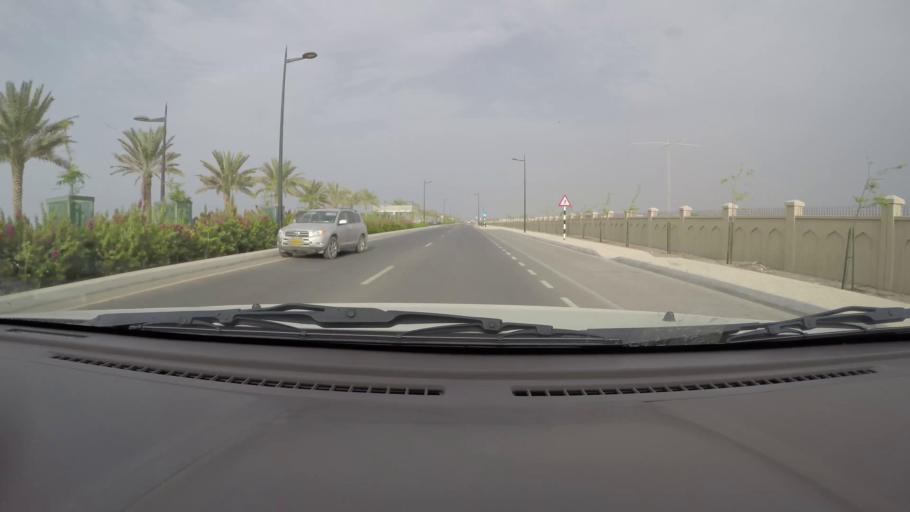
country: OM
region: Muhafazat Masqat
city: As Sib al Jadidah
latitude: 23.6920
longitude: 58.1668
